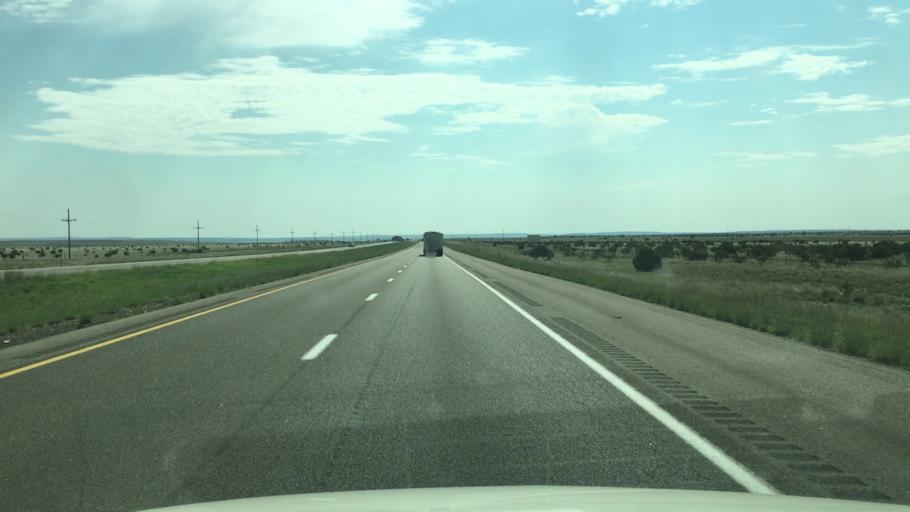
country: US
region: New Mexico
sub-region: Guadalupe County
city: Santa Rosa
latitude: 34.9828
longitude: -105.1207
